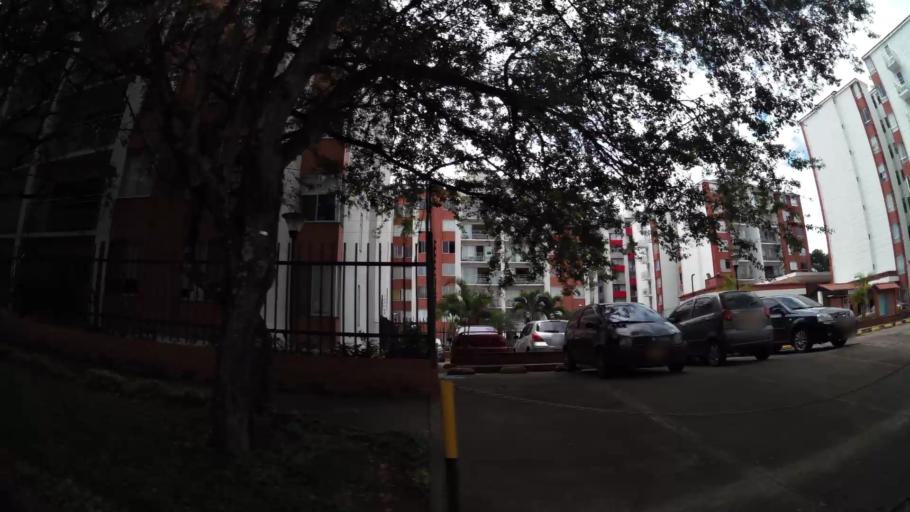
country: CO
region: Valle del Cauca
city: Cali
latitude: 3.3953
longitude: -76.5246
